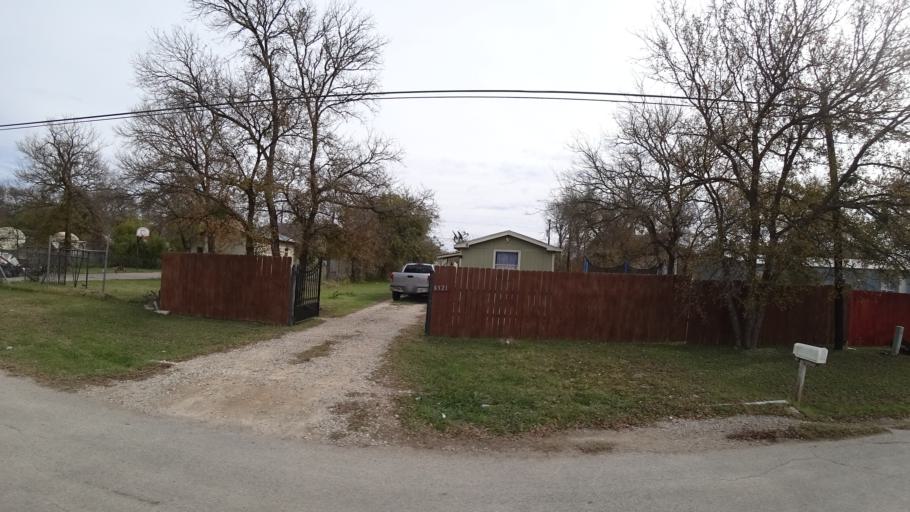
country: US
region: Texas
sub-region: Travis County
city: Garfield
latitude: 30.1329
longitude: -97.5724
